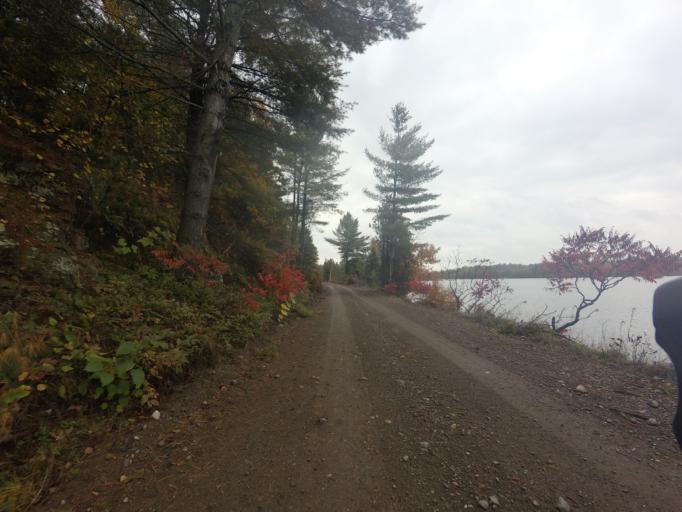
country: CA
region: Ontario
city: Renfrew
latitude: 45.1876
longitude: -76.6869
